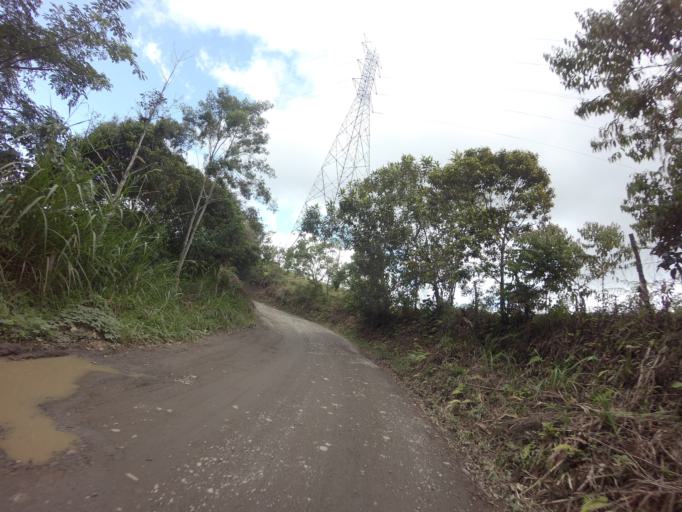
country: CO
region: Caldas
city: Victoria
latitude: 5.3186
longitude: -74.9499
